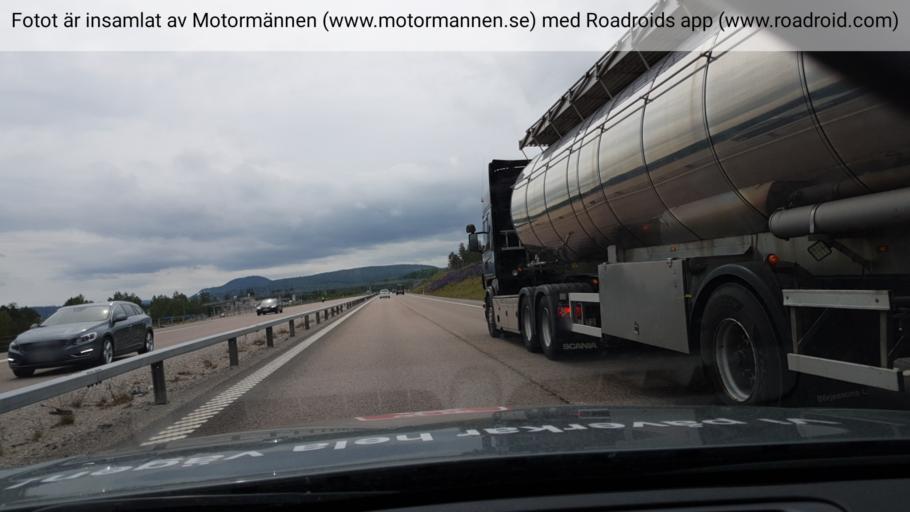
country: SE
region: Vaesternorrland
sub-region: Sundsvalls Kommun
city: Stockvik
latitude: 62.3556
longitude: 17.3649
